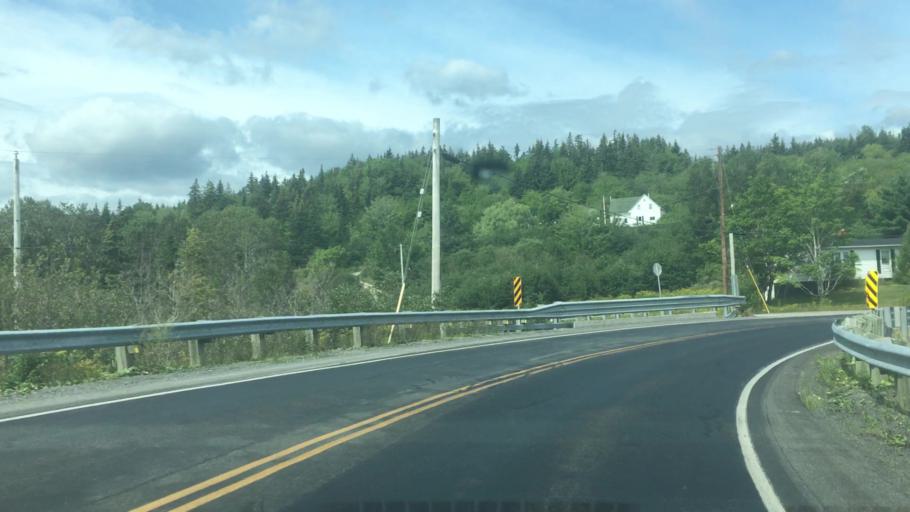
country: CA
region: Nova Scotia
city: Sydney Mines
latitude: 46.2637
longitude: -60.6242
